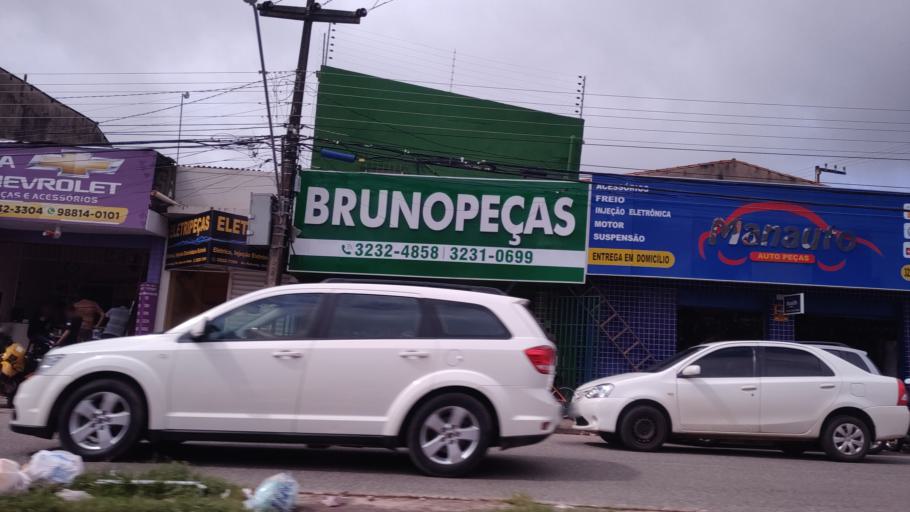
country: BR
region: Maranhao
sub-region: Sao Luis
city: Sao Luis
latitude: -2.5416
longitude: -44.2855
